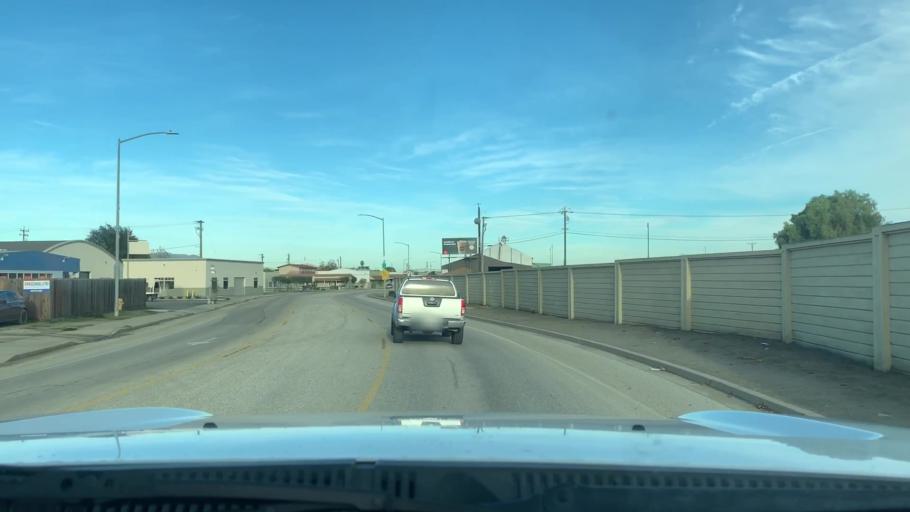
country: US
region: California
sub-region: Monterey County
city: King City
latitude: 36.2117
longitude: -121.1211
